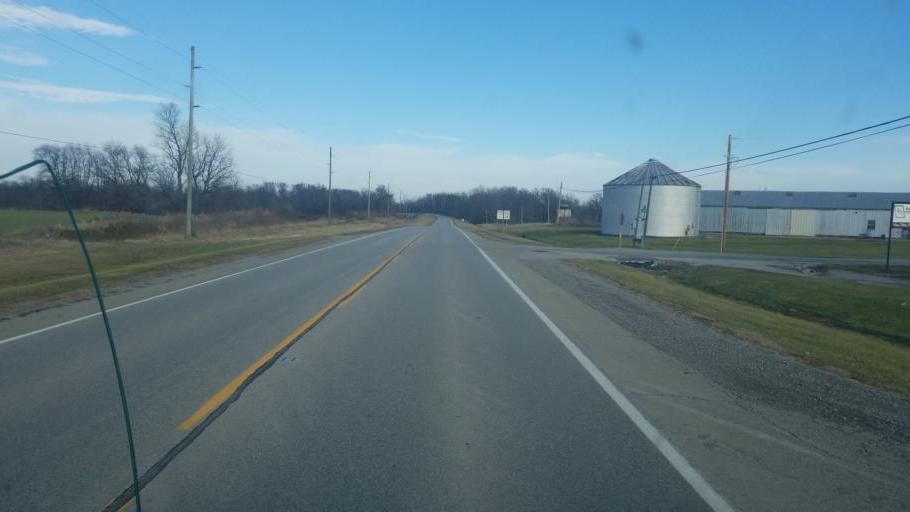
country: US
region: Illinois
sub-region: White County
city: Carmi
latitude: 38.1058
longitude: -88.1310
